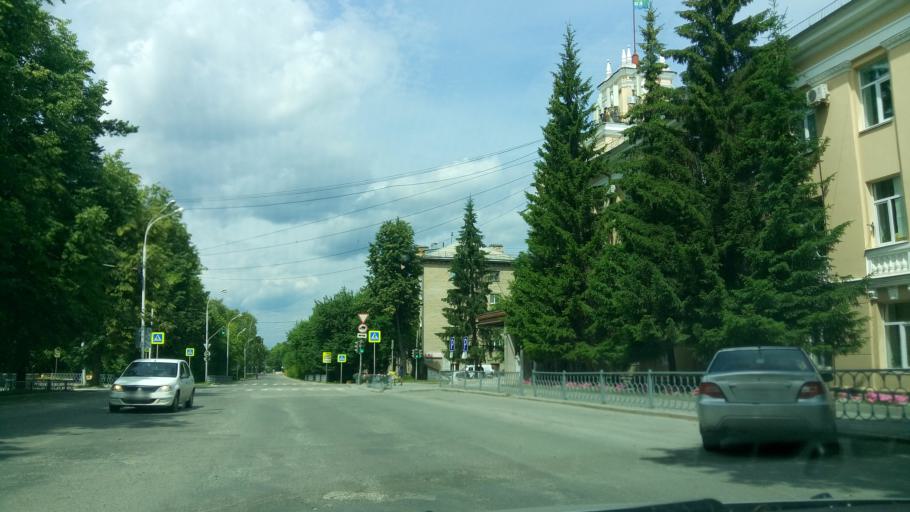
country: RU
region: Sverdlovsk
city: Yekaterinburg
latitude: 56.8866
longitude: 60.6245
